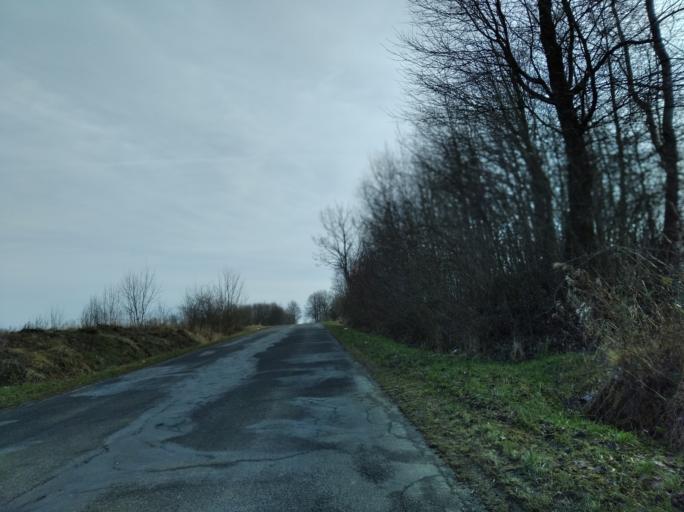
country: PL
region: Subcarpathian Voivodeship
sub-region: Powiat brzozowski
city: Stara Wies
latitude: 49.7140
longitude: 21.9843
